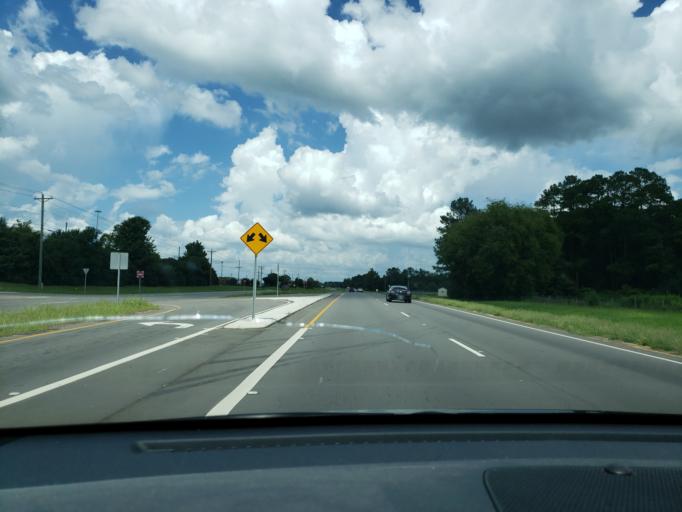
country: US
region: North Carolina
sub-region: Robeson County
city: Saint Pauls
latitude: 34.7450
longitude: -78.8019
